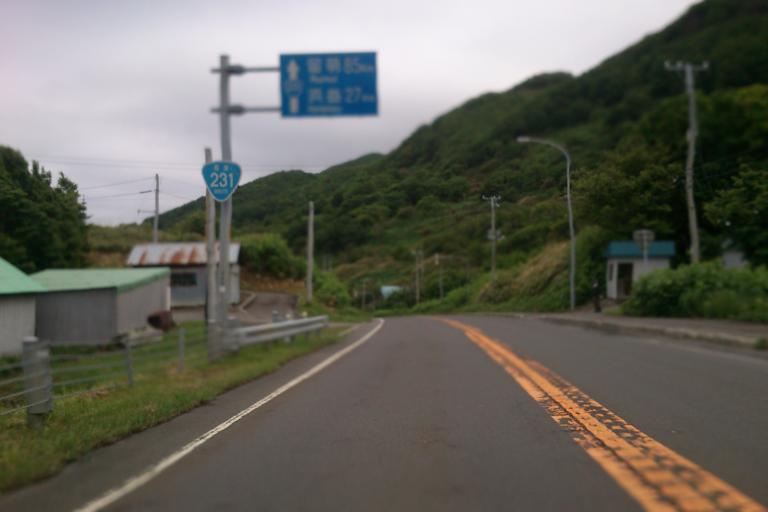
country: JP
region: Hokkaido
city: Ishikari
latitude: 43.4193
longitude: 141.4296
